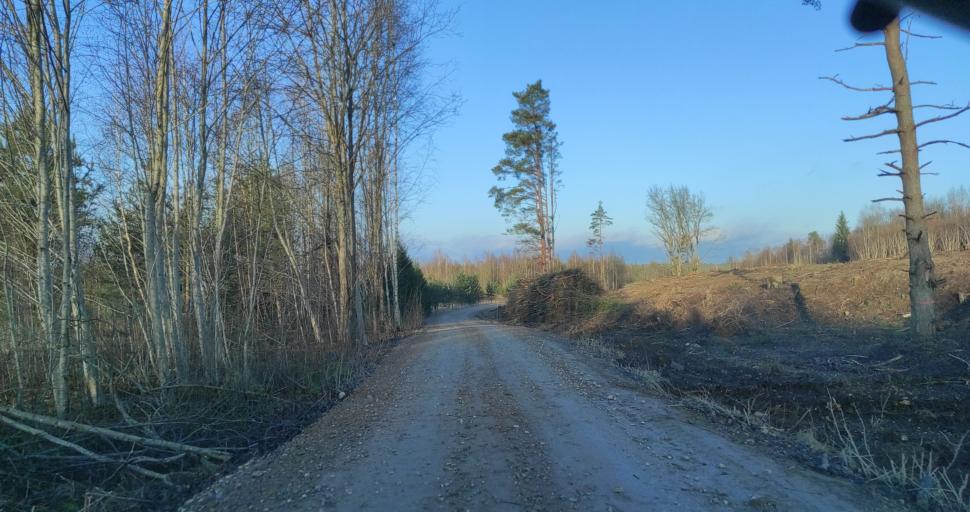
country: LV
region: Kuldigas Rajons
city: Kuldiga
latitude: 57.0486
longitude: 21.8637
